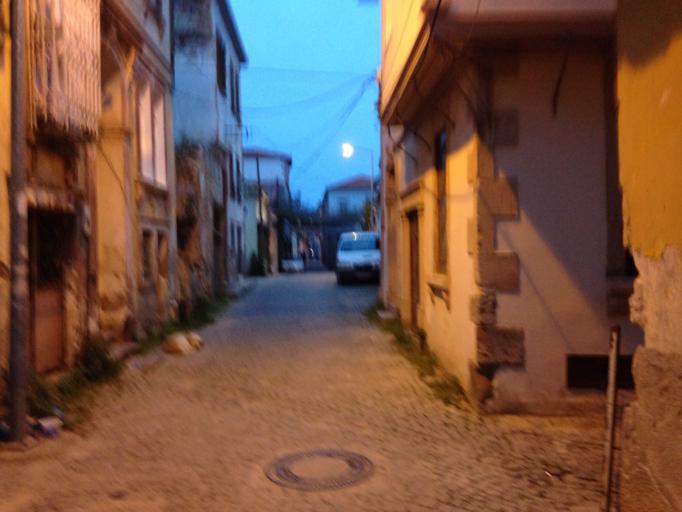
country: TR
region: Balikesir
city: Ayvalik
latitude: 39.3210
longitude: 26.6937
